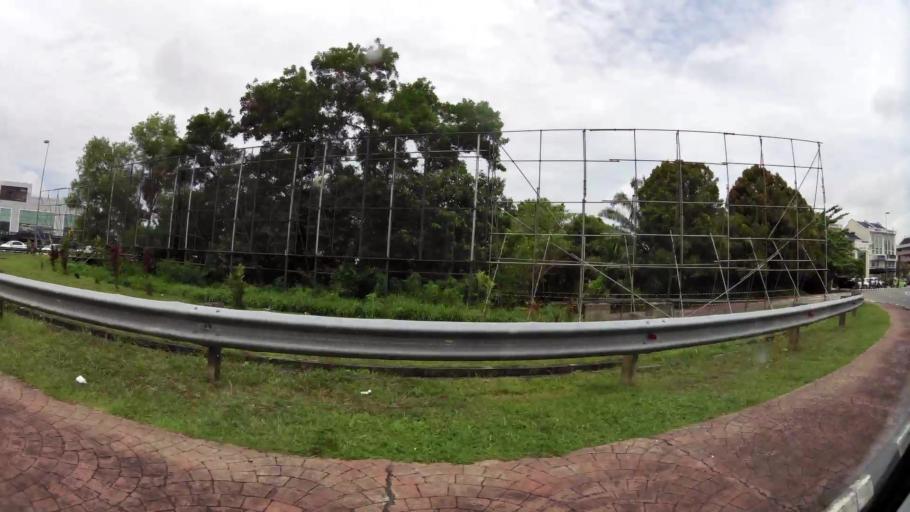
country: BN
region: Brunei and Muara
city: Bandar Seri Begawan
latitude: 4.9011
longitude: 114.9189
